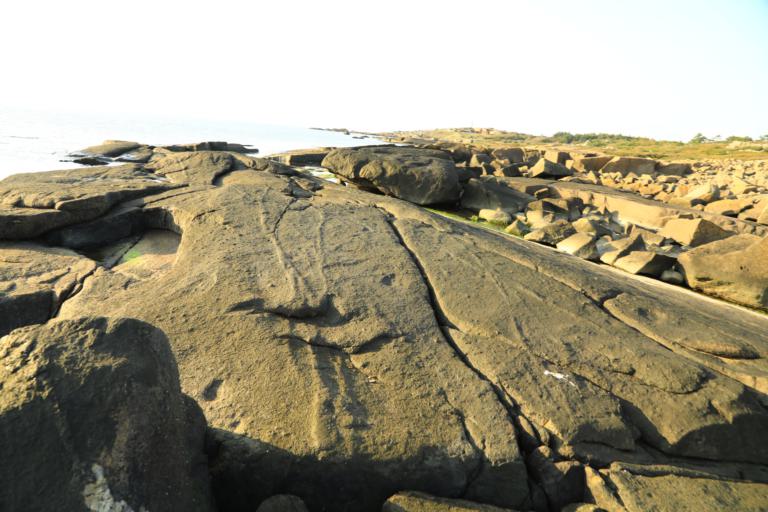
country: SE
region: Halland
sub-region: Varbergs Kommun
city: Varberg
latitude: 57.0834
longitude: 12.2424
